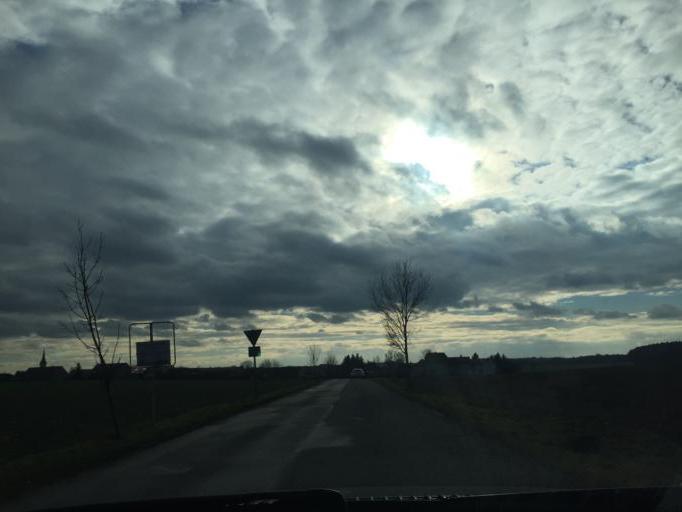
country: DE
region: Saxony
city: Ebersbach
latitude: 51.2065
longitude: 13.6719
